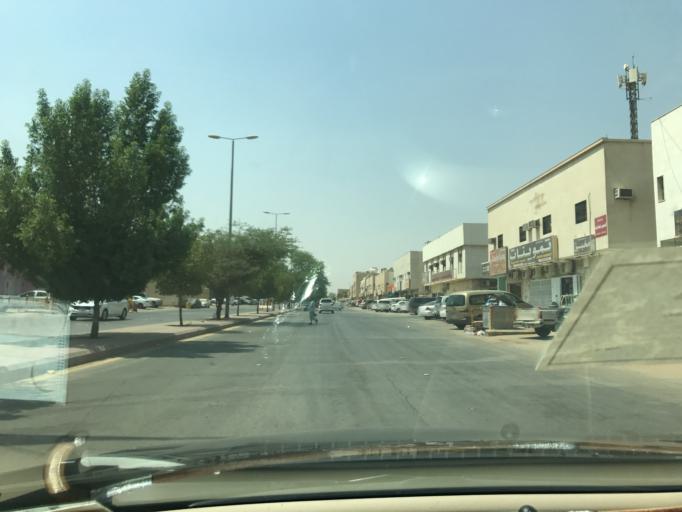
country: SA
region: Ar Riyad
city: Riyadh
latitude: 24.7471
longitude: 46.7719
